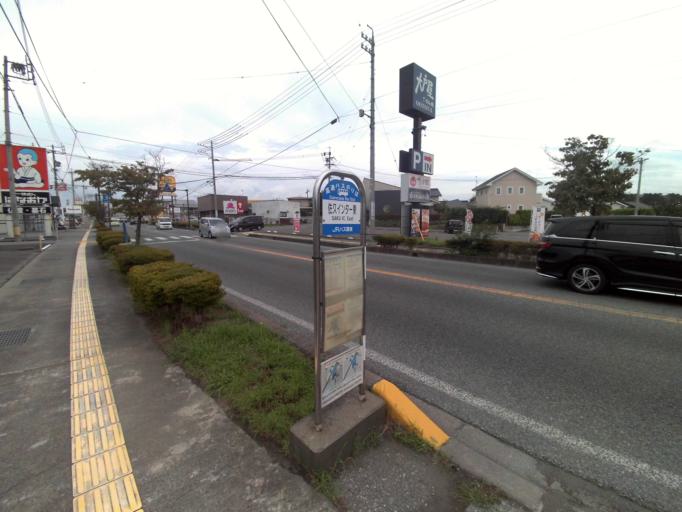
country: JP
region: Nagano
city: Komoro
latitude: 36.2814
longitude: 138.4806
